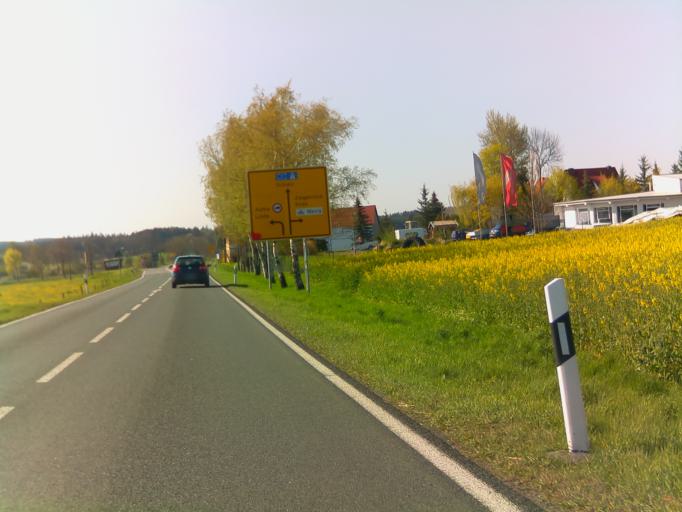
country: DE
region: Thuringia
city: Dreba
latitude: 50.6881
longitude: 11.7776
